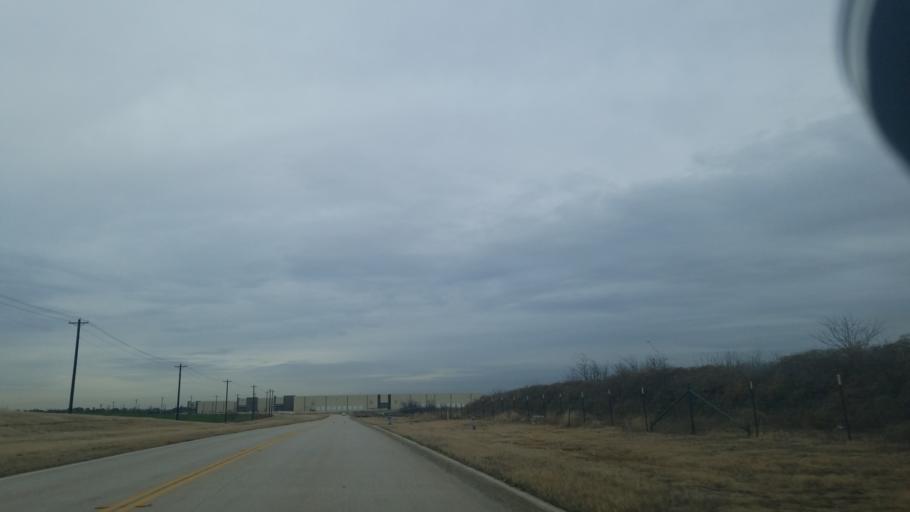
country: US
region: Texas
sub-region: Denton County
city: Denton
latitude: 33.2218
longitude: -97.1859
